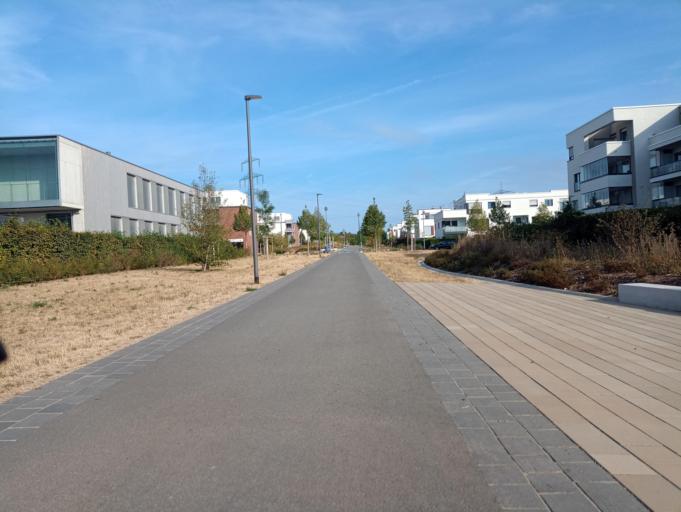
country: DE
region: Hesse
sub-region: Regierungsbezirk Darmstadt
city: Bad Homburg vor der Hoehe
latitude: 50.1801
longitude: 8.6218
